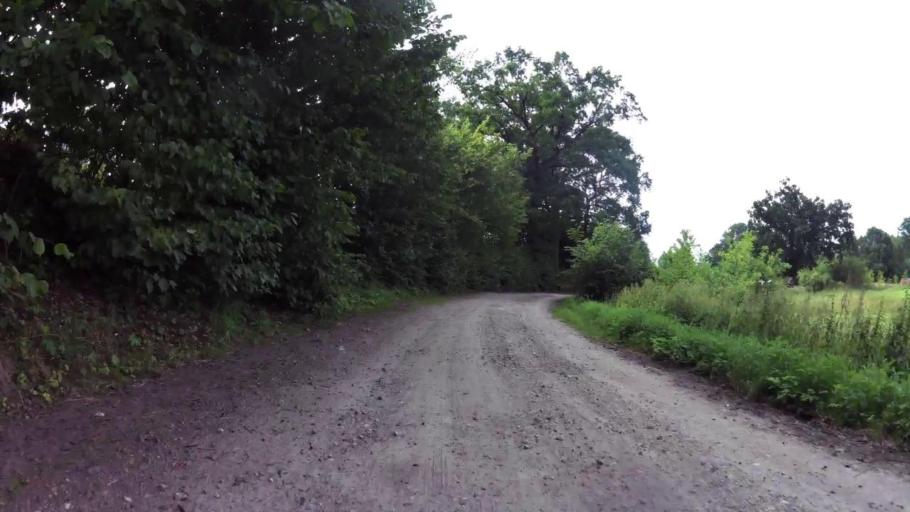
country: PL
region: West Pomeranian Voivodeship
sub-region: Powiat lobeski
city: Wegorzyno
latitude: 53.5341
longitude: 15.6140
